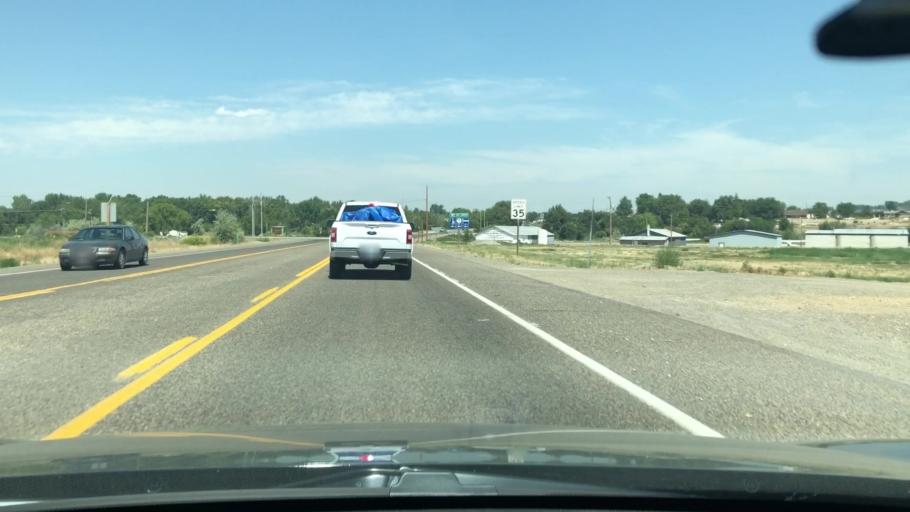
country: US
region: Idaho
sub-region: Owyhee County
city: Homedale
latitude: 43.6161
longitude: -116.9264
